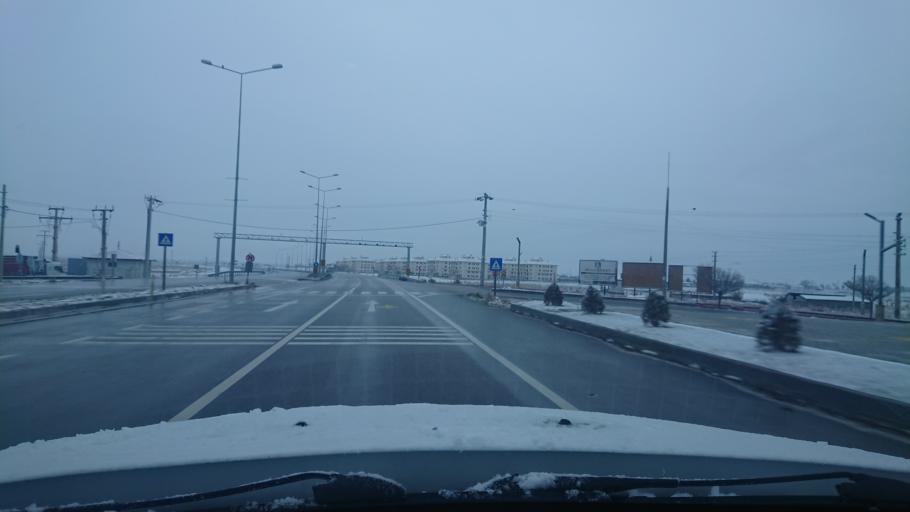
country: TR
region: Aksaray
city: Sultanhani
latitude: 38.2527
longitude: 33.5650
